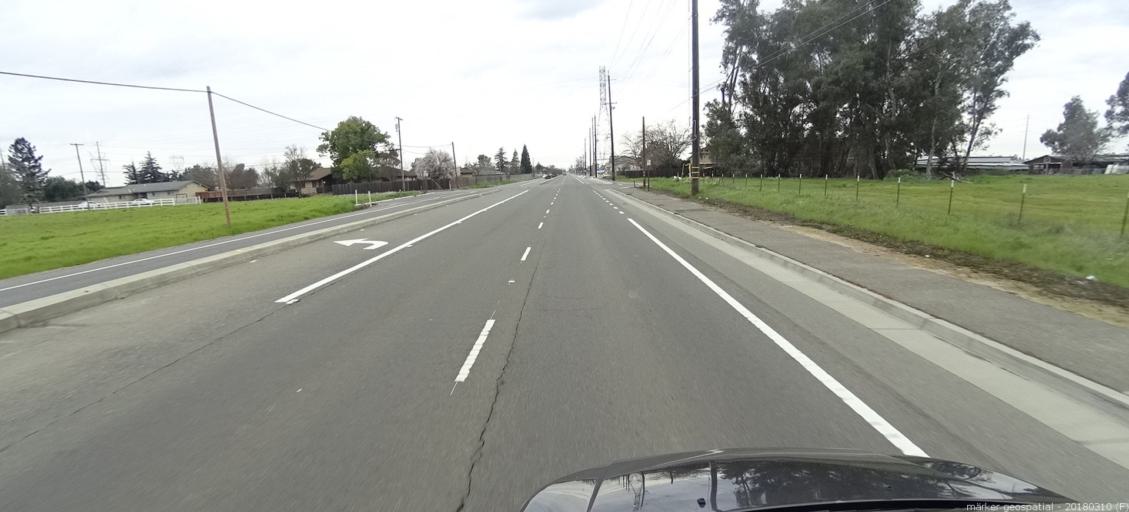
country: US
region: California
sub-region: Sacramento County
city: Vineyard
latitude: 38.4817
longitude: -121.3479
